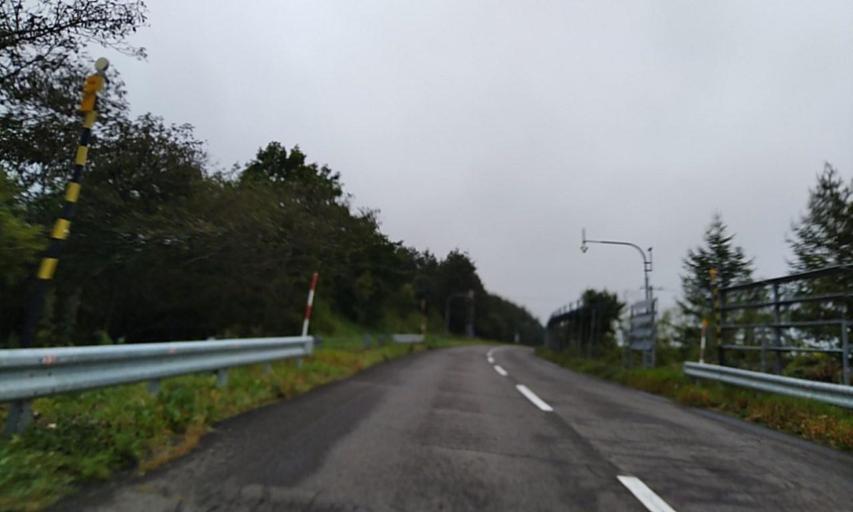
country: JP
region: Hokkaido
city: Shibetsu
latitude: 43.5343
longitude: 144.7055
